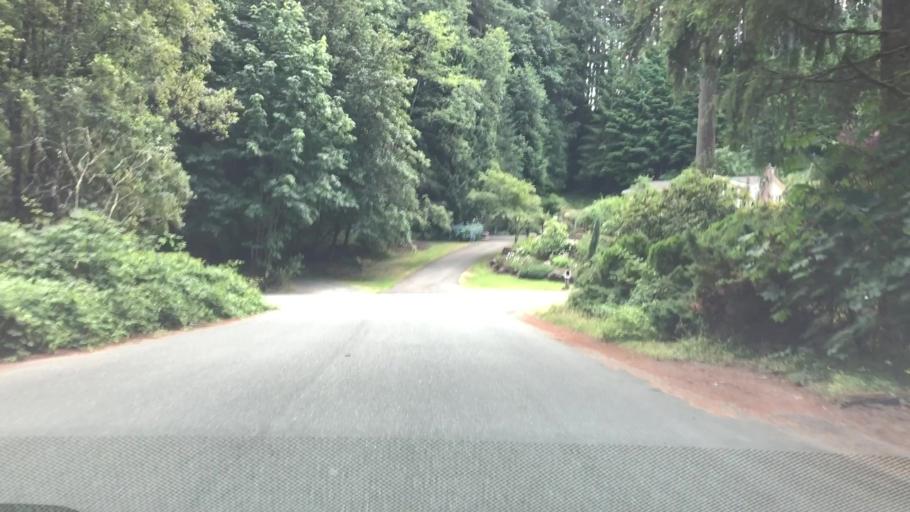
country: US
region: Washington
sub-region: King County
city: Cottage Lake
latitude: 47.7410
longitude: -122.1054
